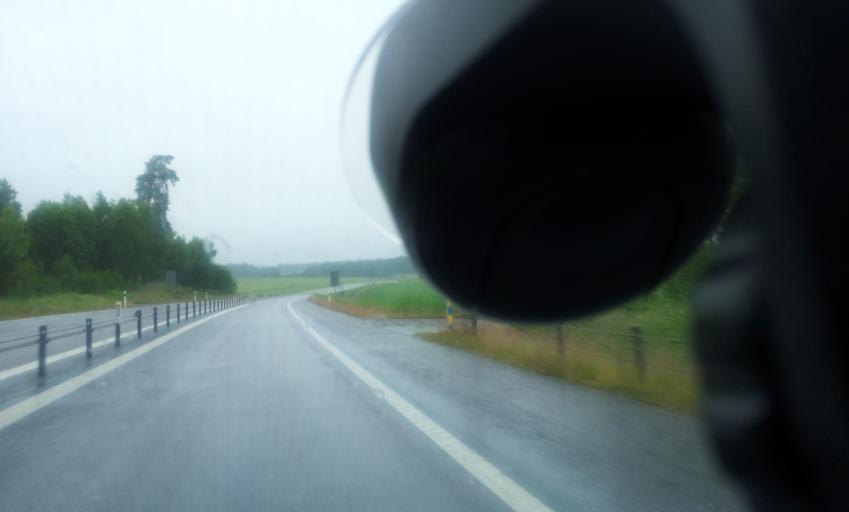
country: SE
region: OEstergoetland
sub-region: Soderkopings Kommun
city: Soederkoeping
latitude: 58.4448
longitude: 16.3674
